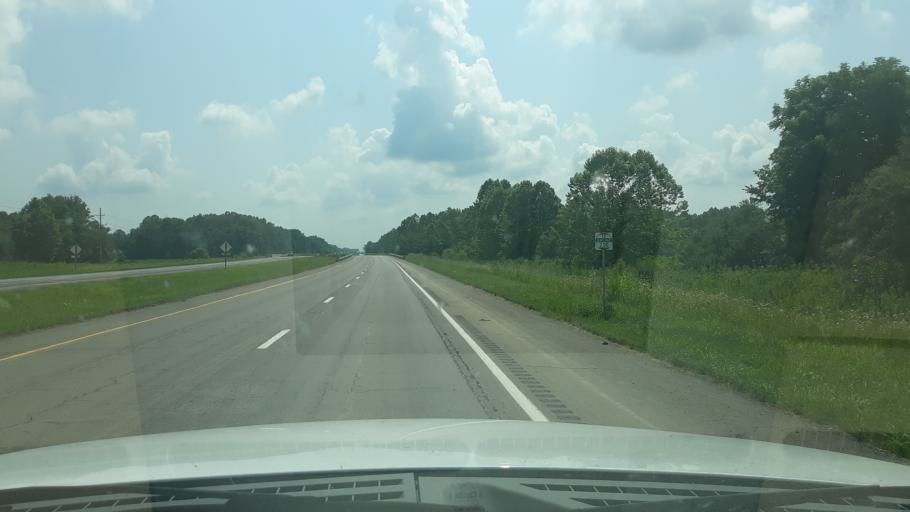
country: US
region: Illinois
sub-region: Saline County
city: Carrier Mills
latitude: 37.7333
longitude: -88.6720
